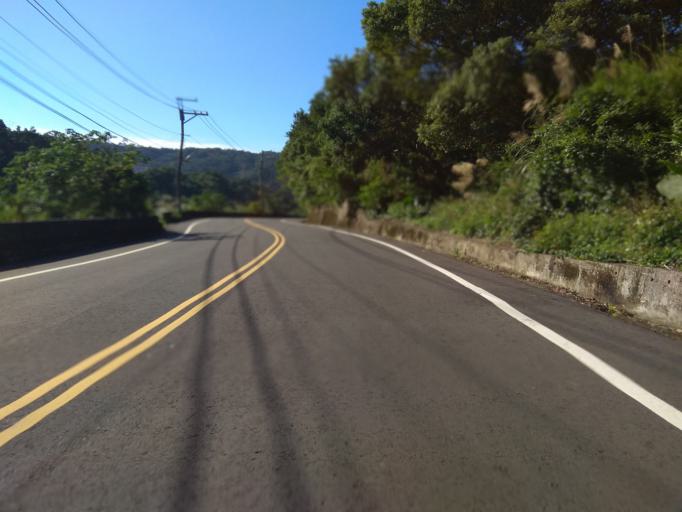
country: TW
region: Taiwan
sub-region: Hsinchu
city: Zhubei
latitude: 24.8502
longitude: 121.1456
